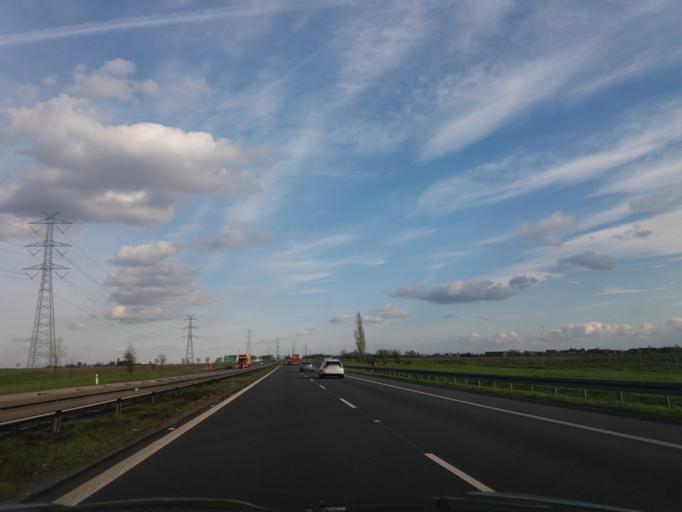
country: PL
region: Lower Silesian Voivodeship
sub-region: Powiat olawski
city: Wierzbno
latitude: 50.9006
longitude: 17.1708
